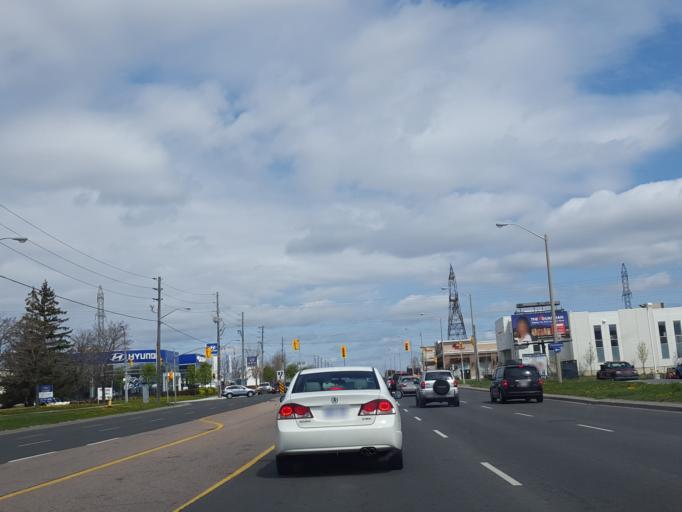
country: CA
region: Ontario
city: Scarborough
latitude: 43.8192
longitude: -79.2457
